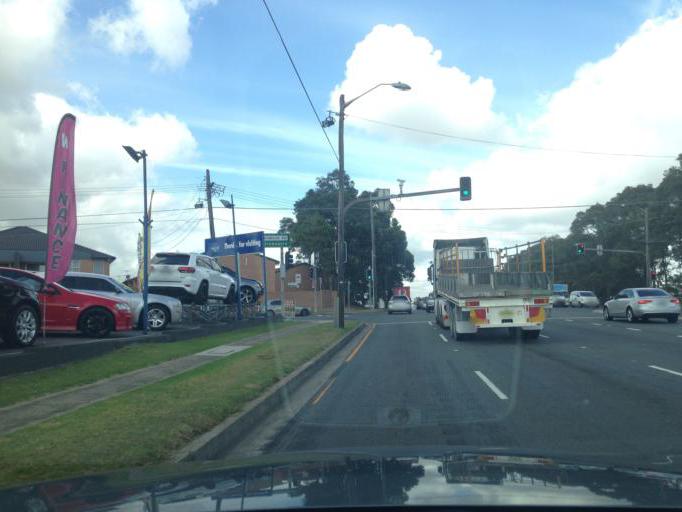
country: AU
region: New South Wales
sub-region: Bankstown
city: Bankstown
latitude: -33.9006
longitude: 151.0460
